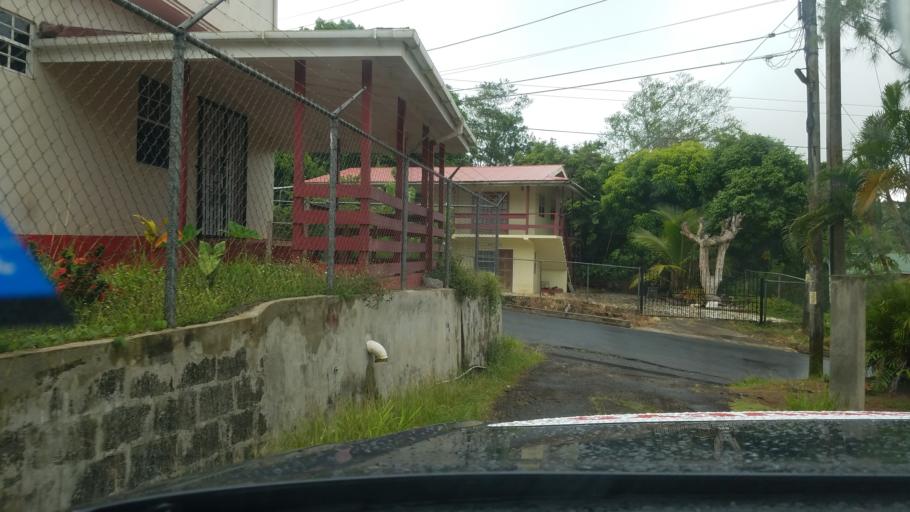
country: LC
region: Castries Quarter
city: Bisee
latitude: 14.0213
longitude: -60.9328
